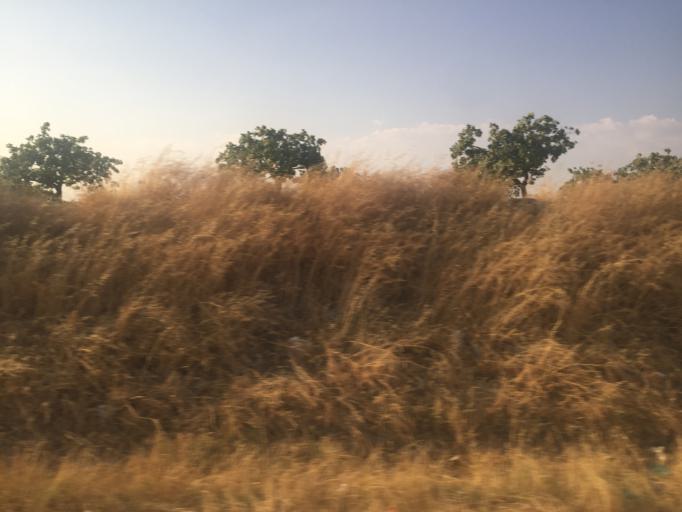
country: TR
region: Sanliurfa
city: Birecik
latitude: 37.0170
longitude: 37.8899
